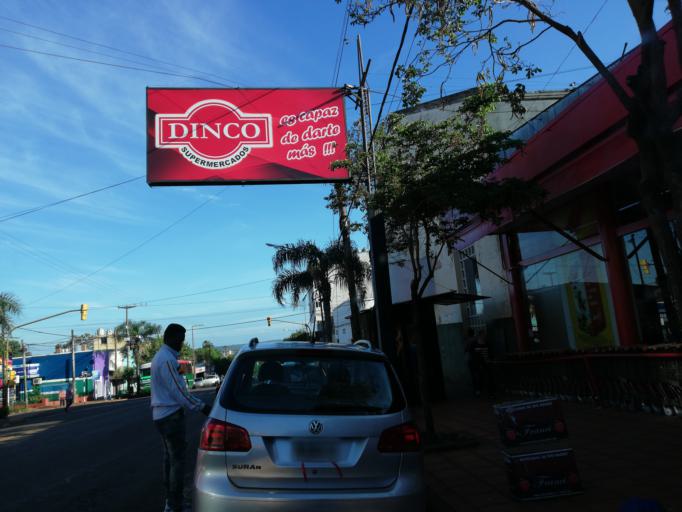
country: AR
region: Misiones
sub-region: Departamento de Obera
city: Obera
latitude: -27.4832
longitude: -55.1211
